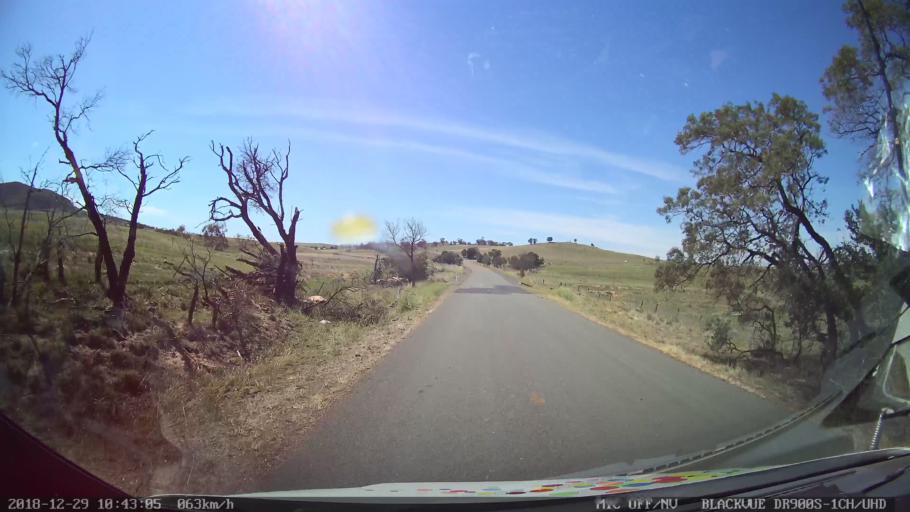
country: AU
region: New South Wales
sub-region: Palerang
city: Bungendore
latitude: -35.0383
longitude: 149.5356
